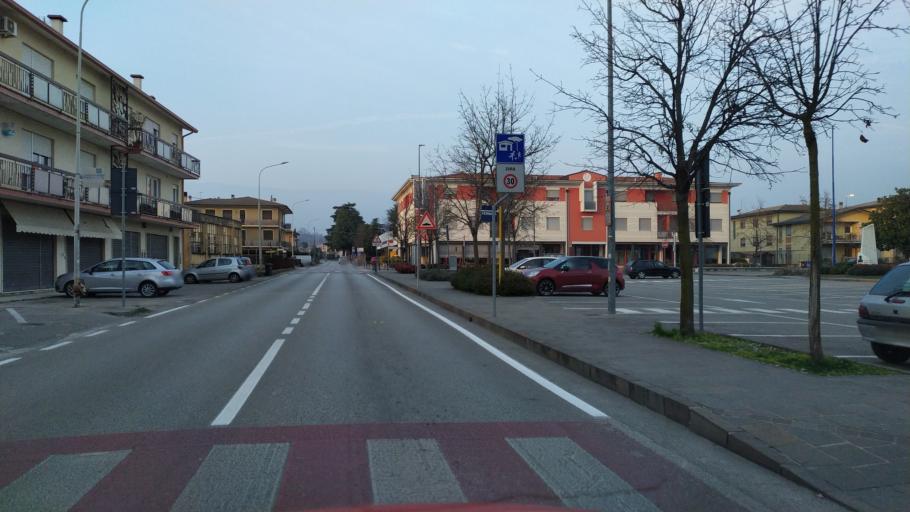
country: IT
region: Veneto
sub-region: Provincia di Vicenza
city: Sarcedo
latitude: 45.6949
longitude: 11.5318
